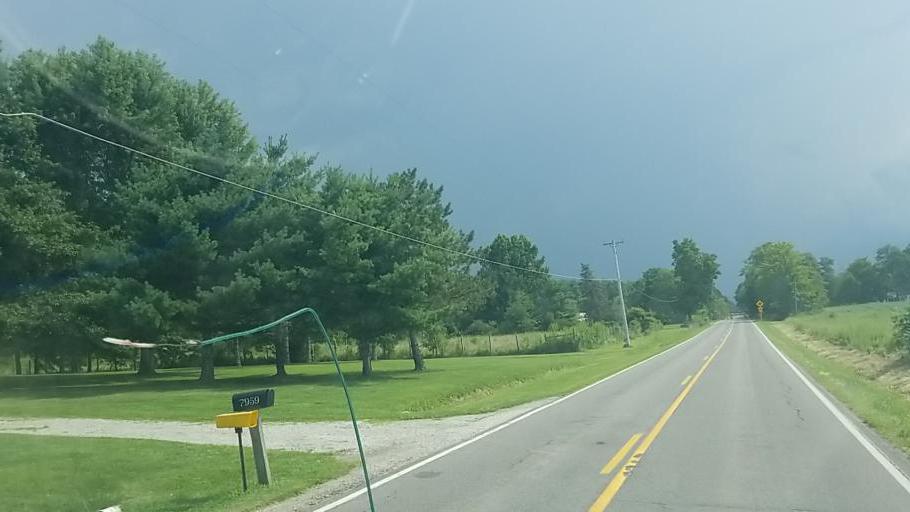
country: US
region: Ohio
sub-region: Medina County
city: Lodi
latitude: 41.0570
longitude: -82.0054
